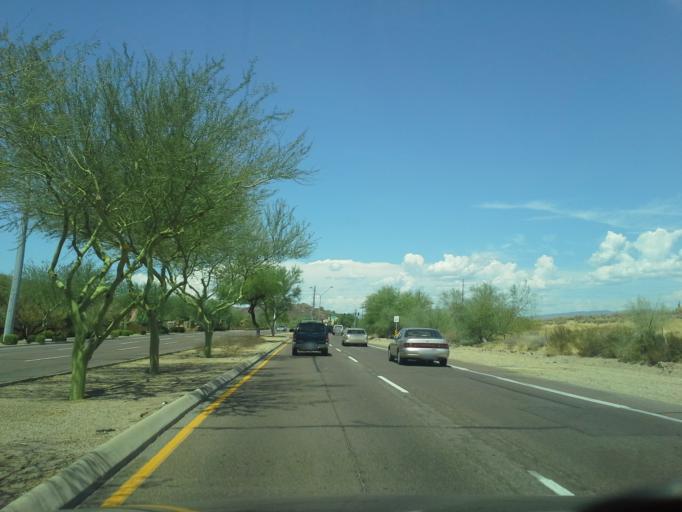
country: US
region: Arizona
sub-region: Maricopa County
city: Cave Creek
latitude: 33.6887
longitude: -112.0312
